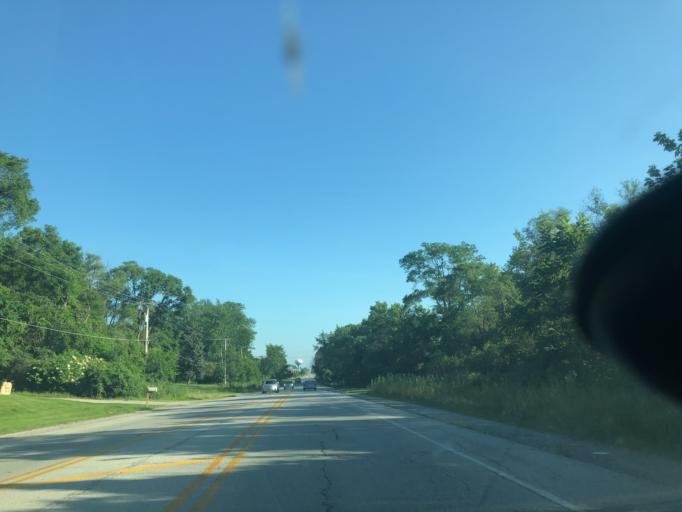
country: US
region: Illinois
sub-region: Cook County
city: Orland Hills
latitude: 41.5850
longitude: -87.8910
